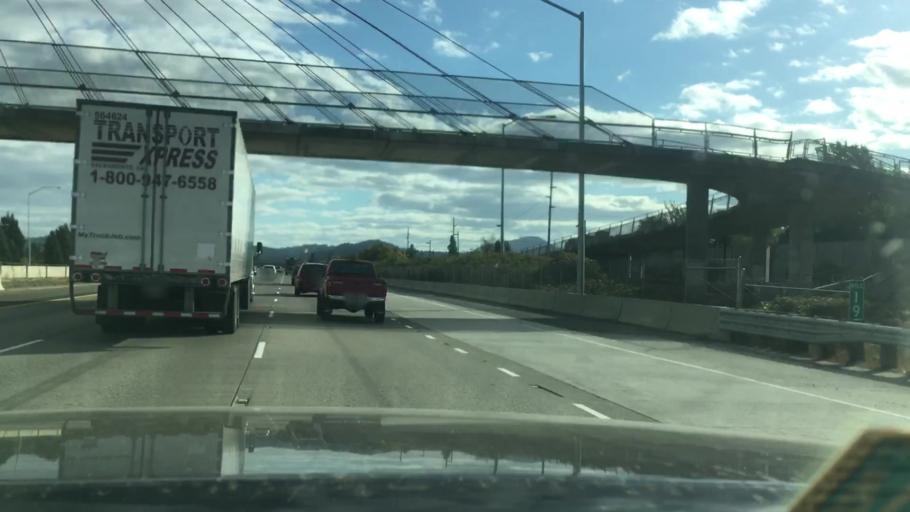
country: US
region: Oregon
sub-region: Lane County
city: Springfield
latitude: 44.0783
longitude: -123.0480
